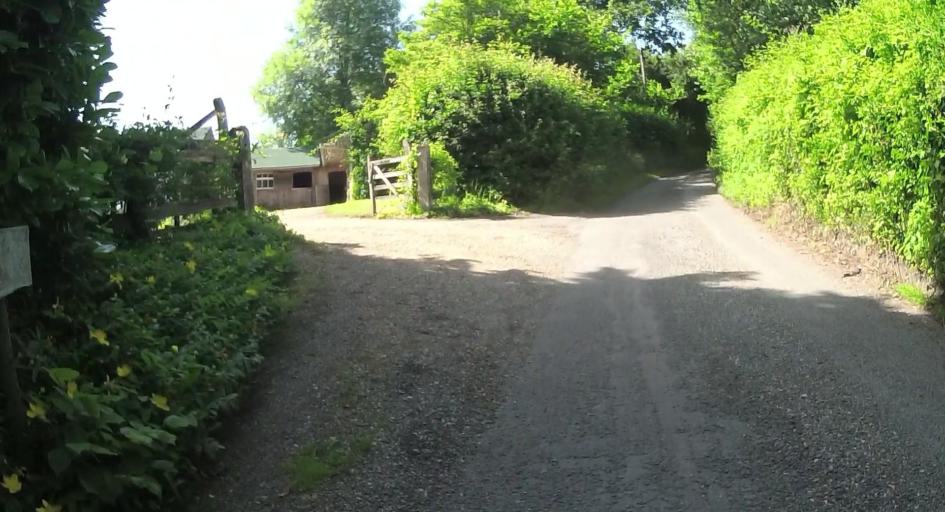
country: GB
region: England
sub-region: Hampshire
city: Kingsley
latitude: 51.1466
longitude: -0.8890
